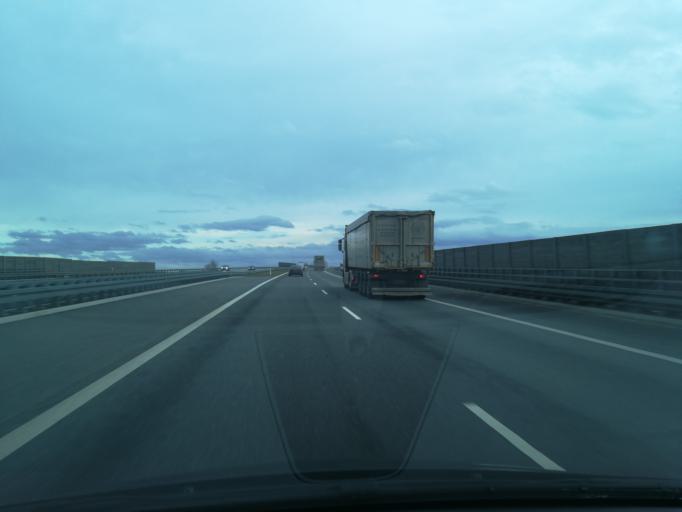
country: PL
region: Kujawsko-Pomorskie
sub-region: Powiat wloclawski
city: Brzesc Kujawski
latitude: 52.6006
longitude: 18.9858
